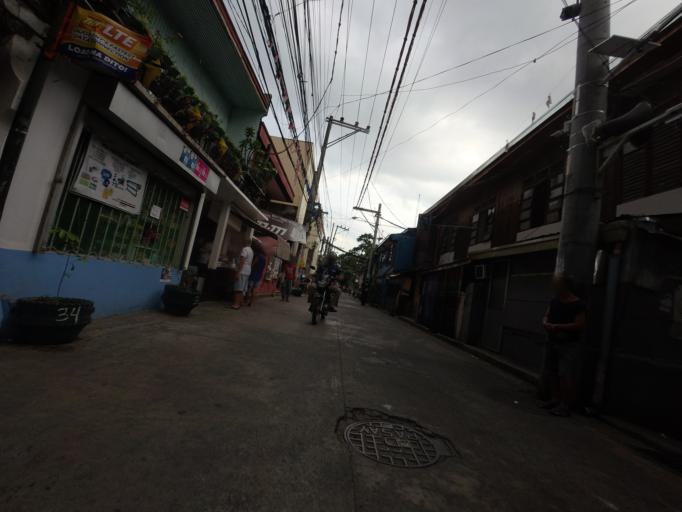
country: PH
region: Metro Manila
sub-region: City of Manila
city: Port Area
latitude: 14.5562
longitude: 120.9939
